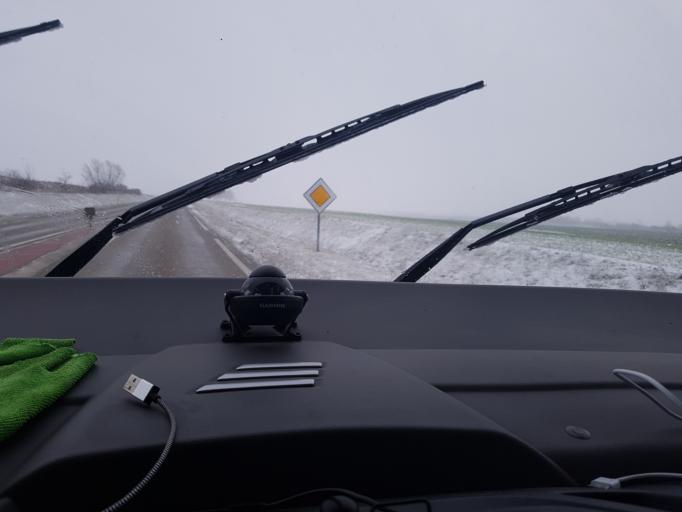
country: FR
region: Lorraine
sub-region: Departement de la Moselle
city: Solgne
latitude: 48.9026
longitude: 6.3491
